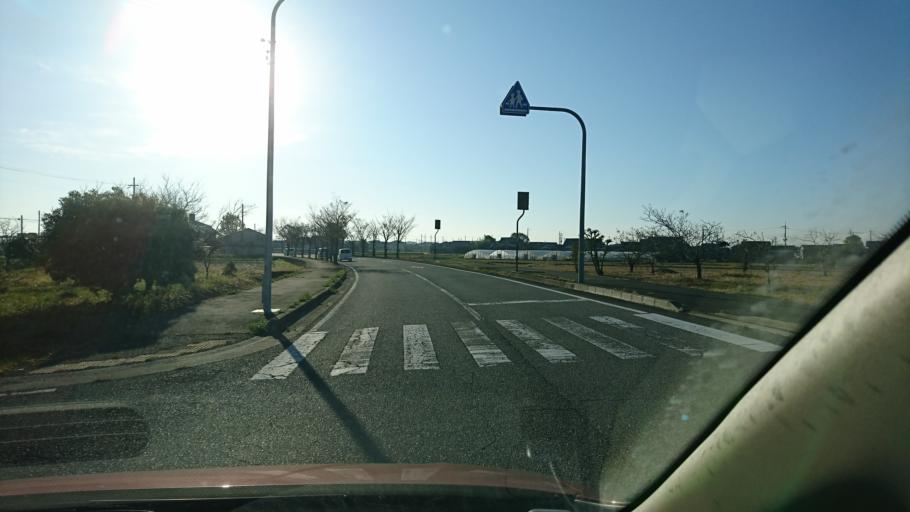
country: JP
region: Hyogo
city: Miki
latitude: 34.7676
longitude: 134.9124
